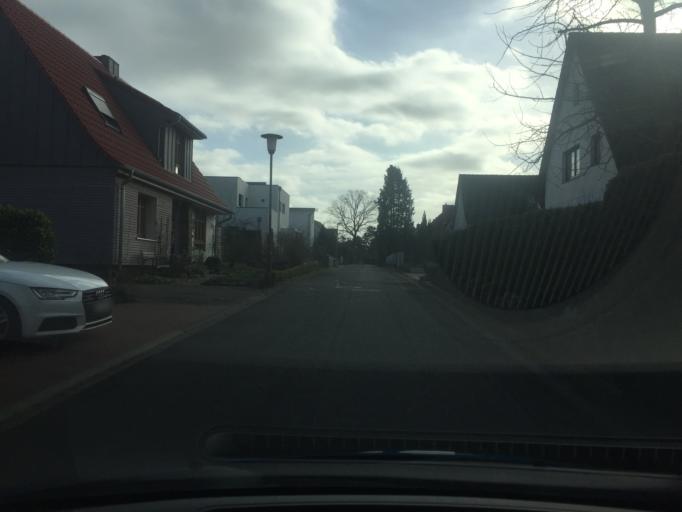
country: DE
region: Lower Saxony
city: Lueneburg
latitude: 53.2348
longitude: 10.4288
